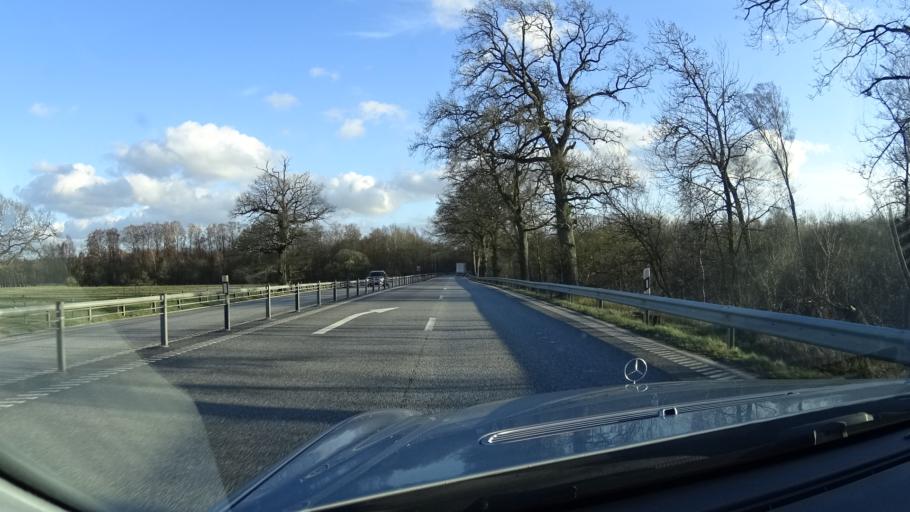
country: SE
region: Skane
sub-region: Hoors Kommun
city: Satofta
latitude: 55.8924
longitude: 13.5238
